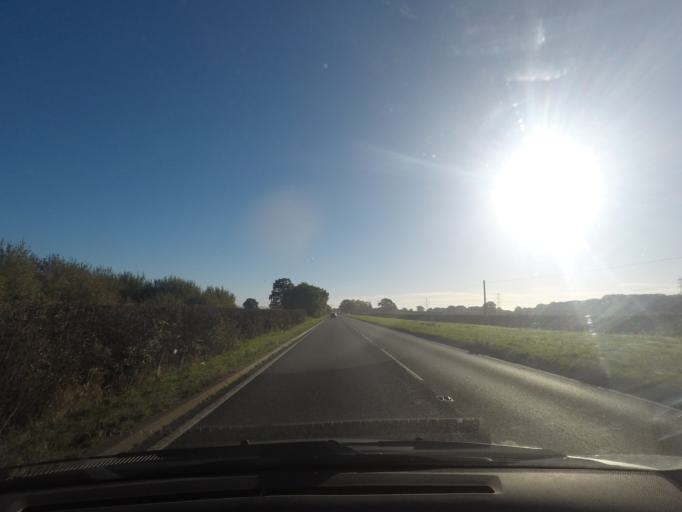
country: GB
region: England
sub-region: City of York
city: Holtby
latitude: 53.9528
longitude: -0.9566
